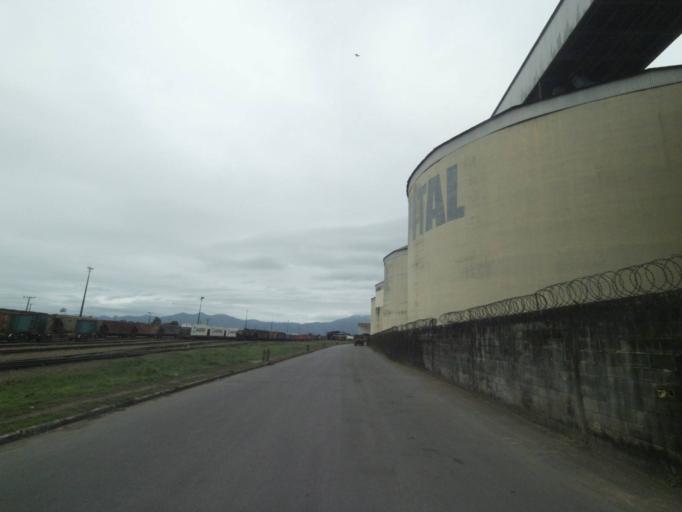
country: BR
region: Parana
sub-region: Paranagua
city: Paranagua
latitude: -25.5407
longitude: -48.5400
